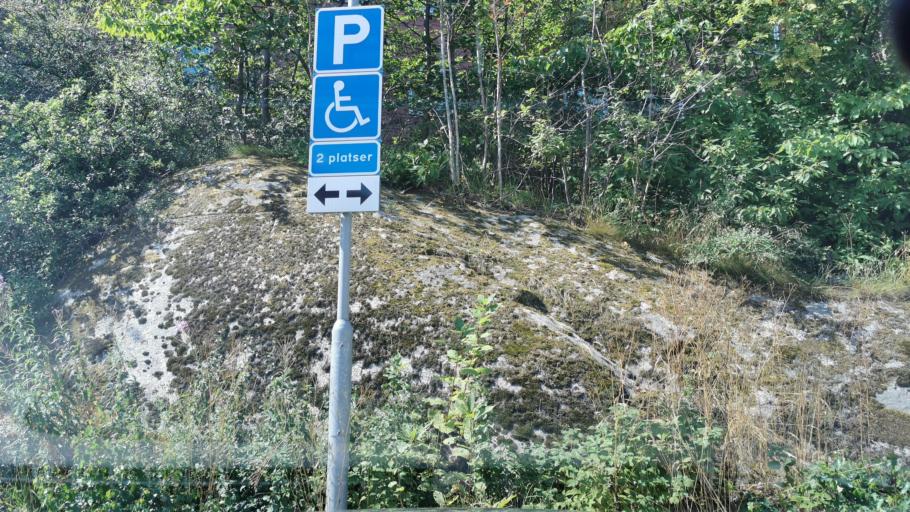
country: SE
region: Vaestra Goetaland
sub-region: Goteborg
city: Majorna
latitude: 57.6622
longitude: 11.9168
